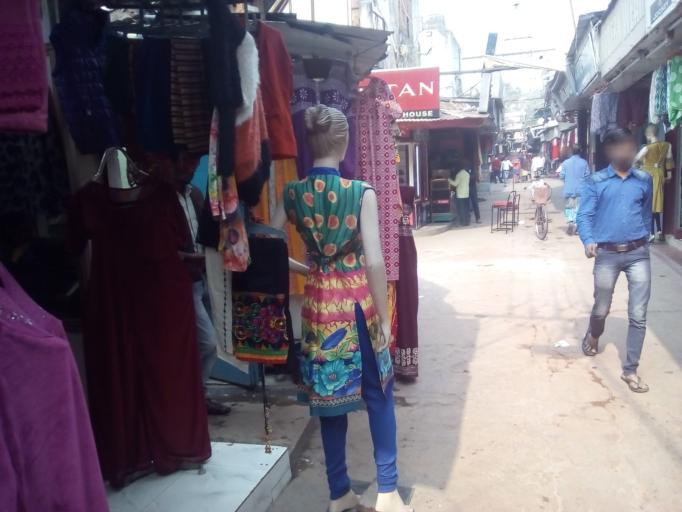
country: IN
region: Bihar
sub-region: Patna
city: Patna
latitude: 25.6186
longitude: 85.1578
